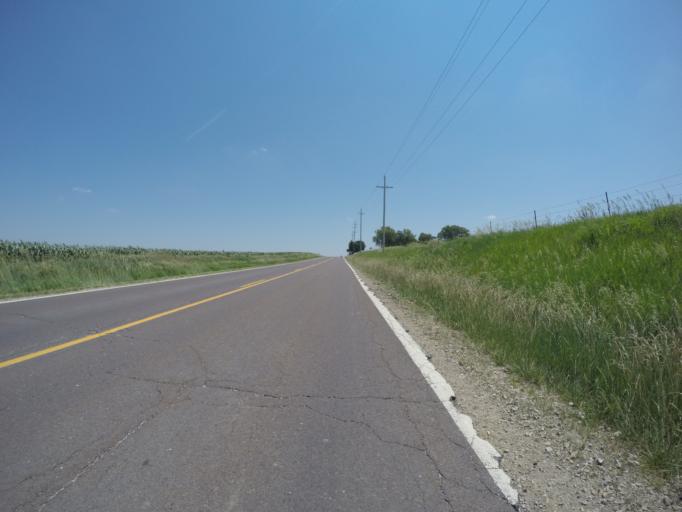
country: US
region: Kansas
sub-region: Doniphan County
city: Troy
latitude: 39.7401
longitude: -95.1899
